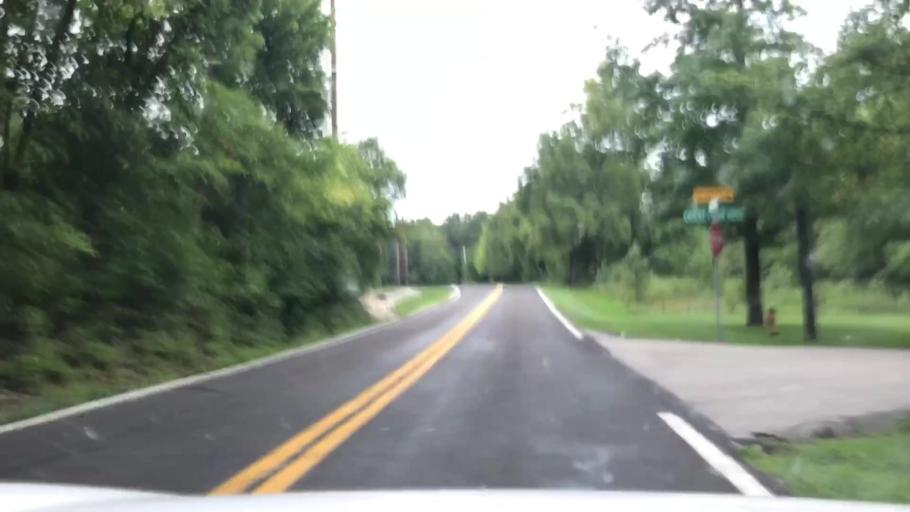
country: US
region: Missouri
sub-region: Saint Louis County
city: Clarkson Valley
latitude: 38.6397
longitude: -90.6111
